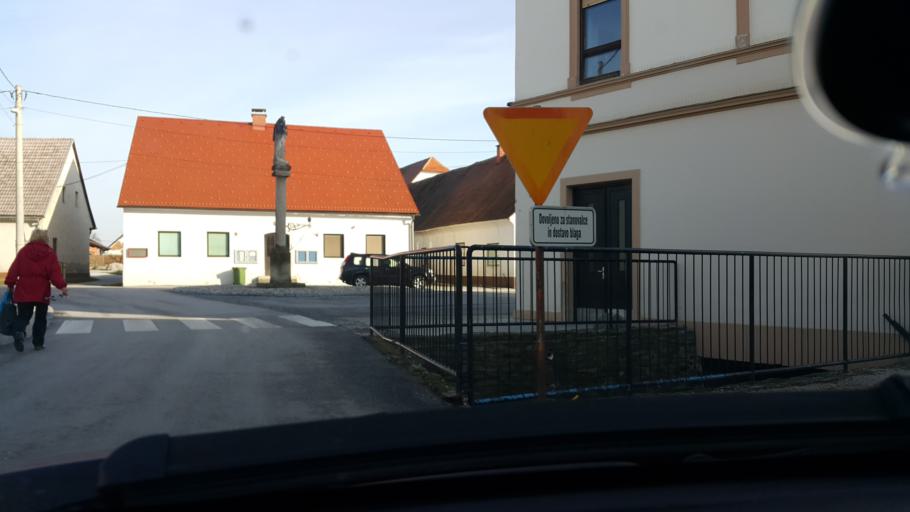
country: SI
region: Slovenska Bistrica
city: Zgornja Polskava
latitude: 46.4132
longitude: 15.6367
